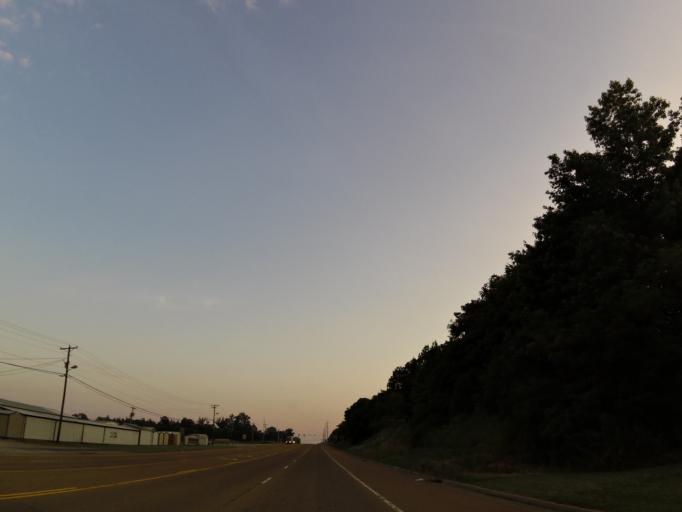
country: US
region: Tennessee
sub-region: Henry County
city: Paris
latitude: 36.2733
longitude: -88.3315
